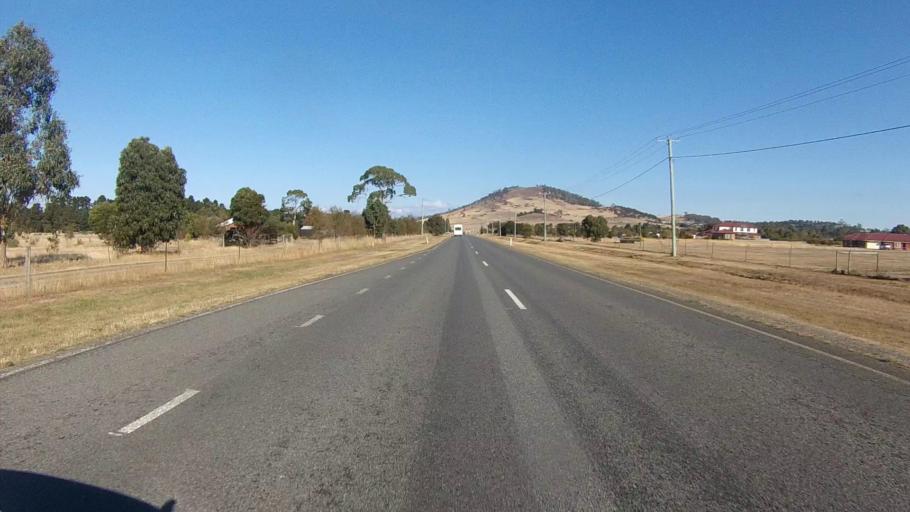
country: AU
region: Tasmania
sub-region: Clarence
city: Seven Mile Beach
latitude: -42.8545
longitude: 147.4880
